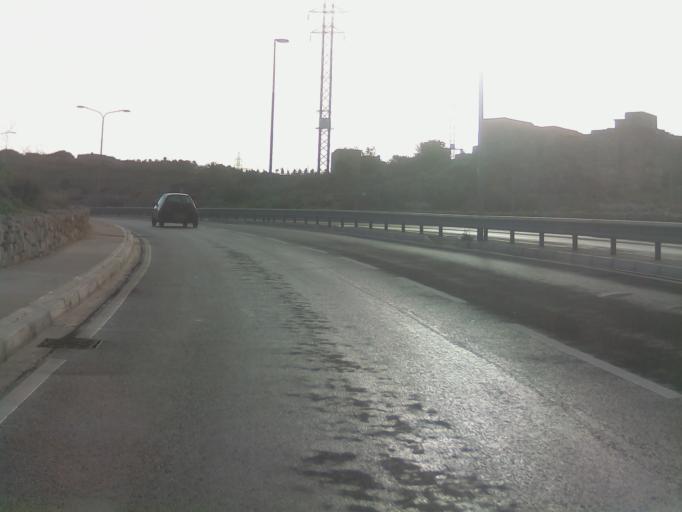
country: MT
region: Il-Mellieha
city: Mellieha
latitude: 35.9553
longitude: 14.3543
